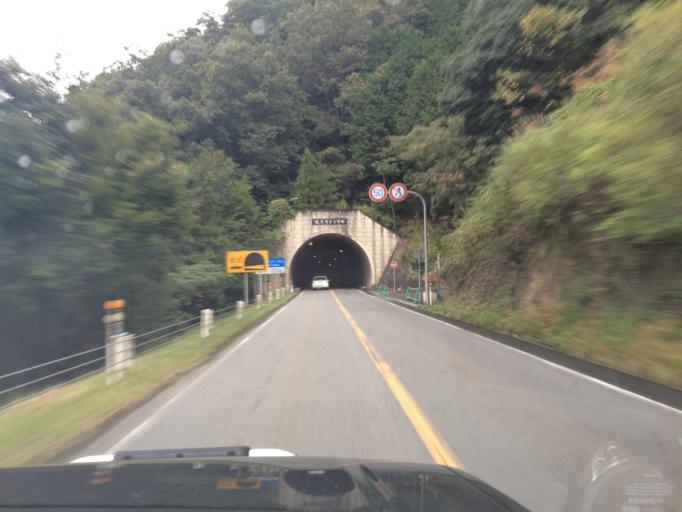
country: JP
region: Hyogo
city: Toyooka
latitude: 35.4425
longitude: 134.7900
